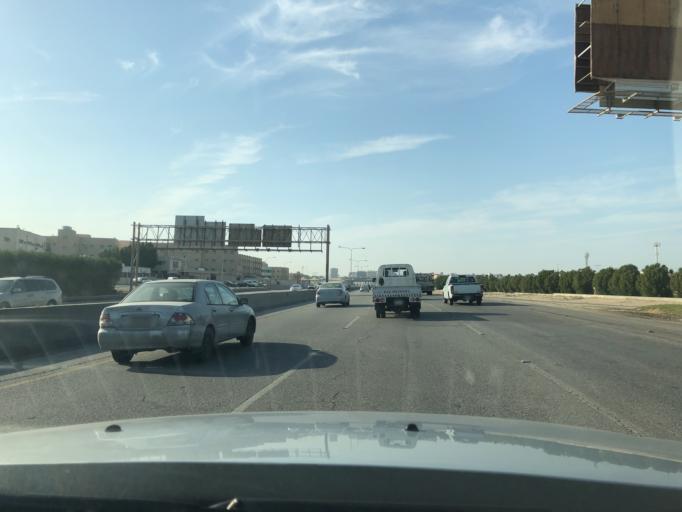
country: SA
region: Eastern Province
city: Dhahran
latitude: 26.3234
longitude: 50.1483
